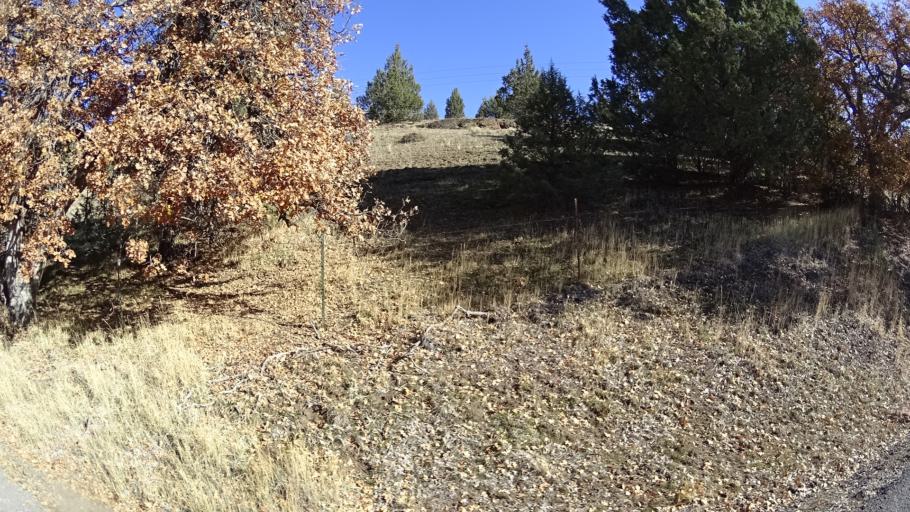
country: US
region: California
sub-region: Siskiyou County
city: Montague
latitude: 41.7911
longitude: -122.3608
